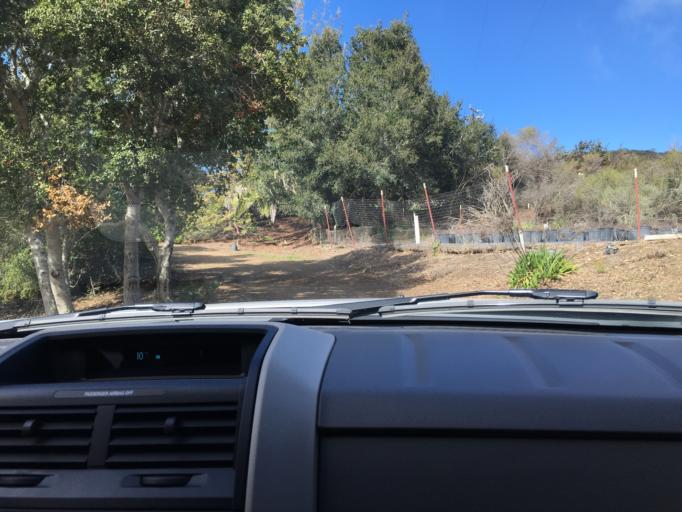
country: US
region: California
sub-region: San Luis Obispo County
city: Los Osos
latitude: 35.2892
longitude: -120.8031
